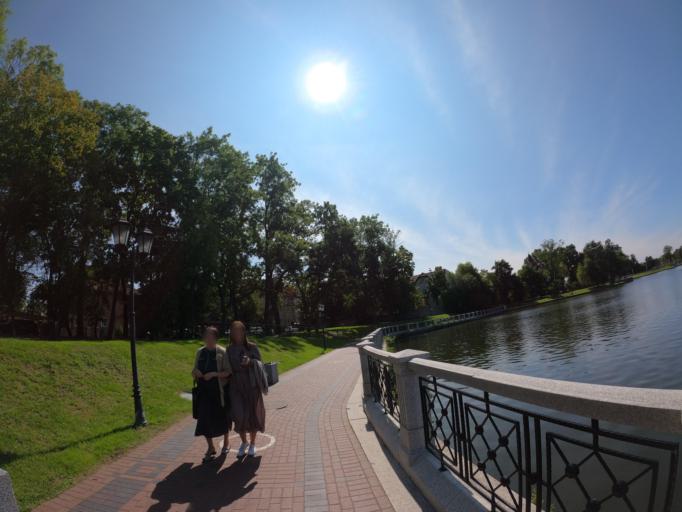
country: RU
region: Kaliningrad
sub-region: Gorod Kaliningrad
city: Kaliningrad
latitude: 54.7298
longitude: 20.5244
